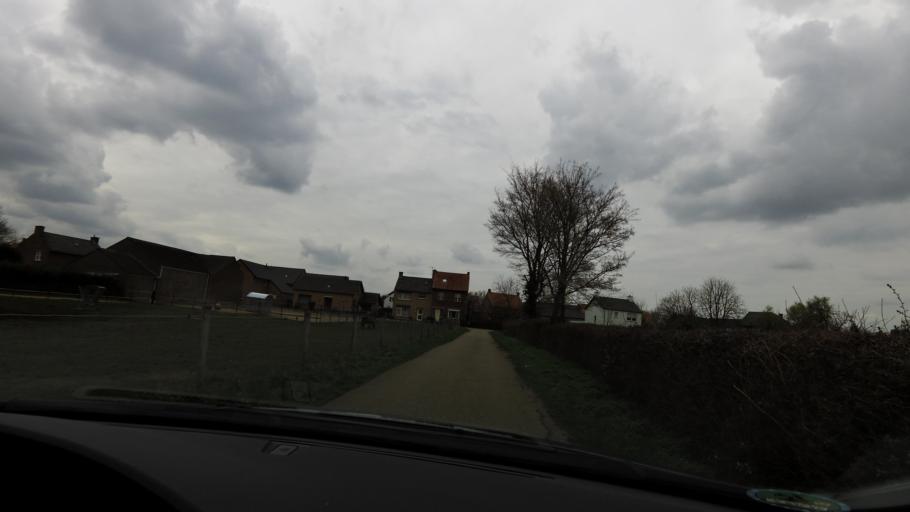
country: NL
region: Limburg
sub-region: Gemeente Sittard-Geleen
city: Born
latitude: 51.0447
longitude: 5.7768
